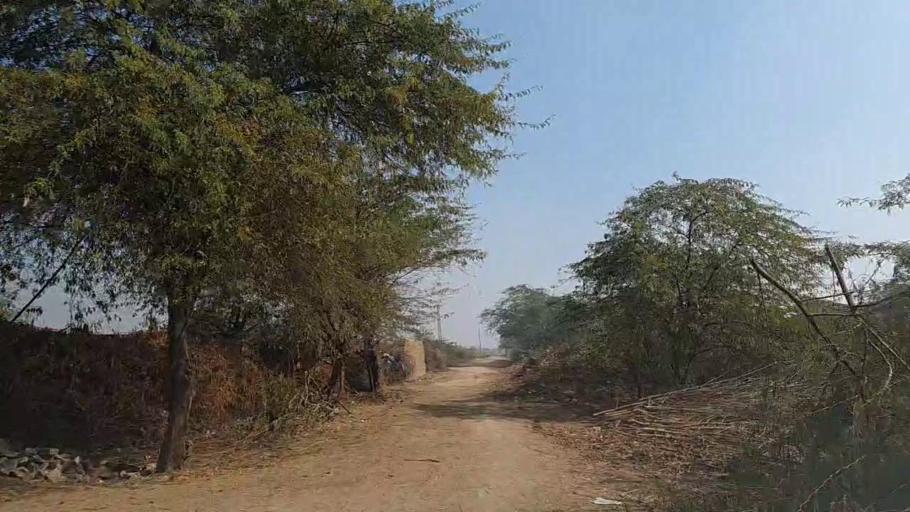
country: PK
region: Sindh
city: Daur
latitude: 26.5011
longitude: 68.3109
